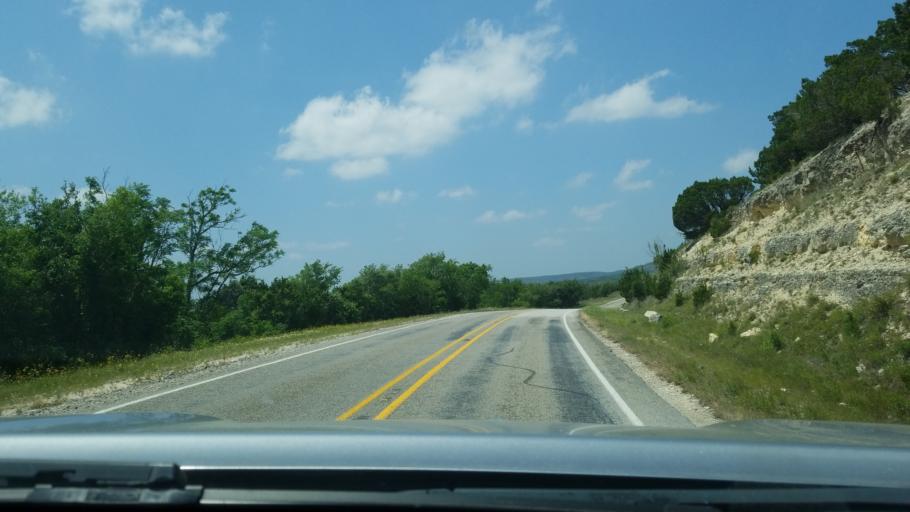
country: US
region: Texas
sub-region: Hays County
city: Woodcreek
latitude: 30.0944
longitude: -98.2357
